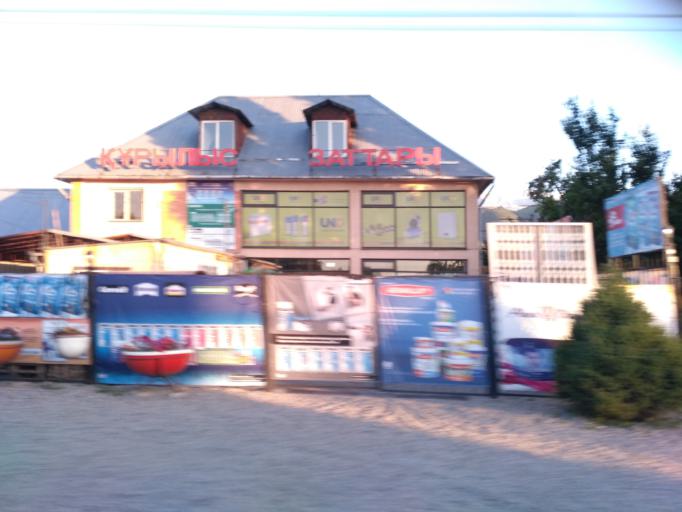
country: KZ
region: Almaty Qalasy
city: Almaty
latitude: 43.1776
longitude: 76.7457
